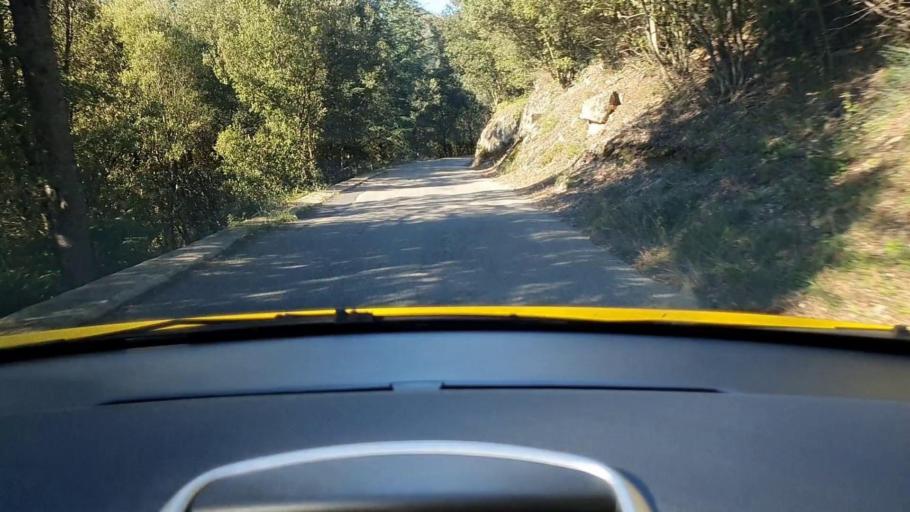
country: FR
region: Languedoc-Roussillon
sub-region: Departement du Gard
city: Valleraugue
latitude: 44.0513
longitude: 3.6972
